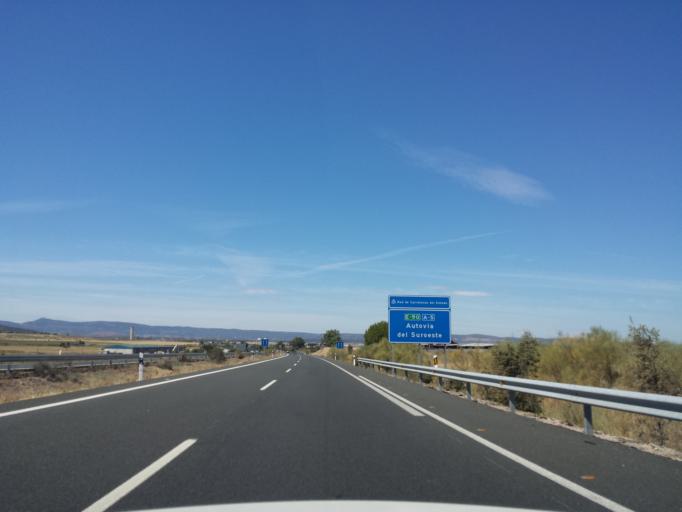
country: ES
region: Extremadura
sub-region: Provincia de Caceres
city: Saucedilla
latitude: 39.8480
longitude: -5.6336
